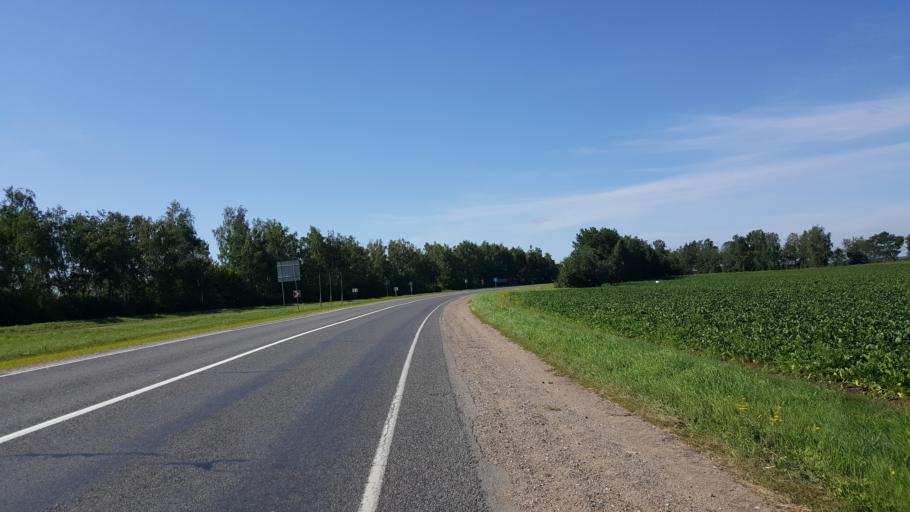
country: BY
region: Brest
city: Kamyanyets
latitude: 52.3701
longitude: 23.7920
